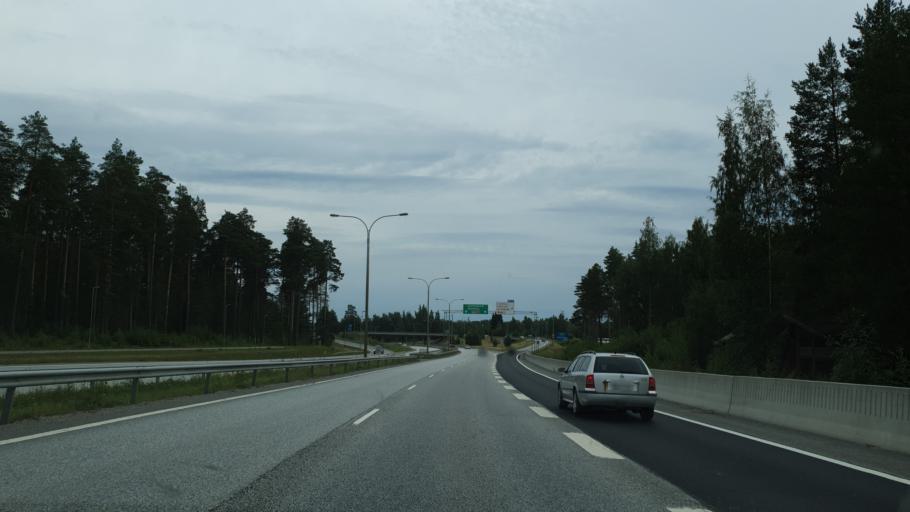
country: FI
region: North Karelia
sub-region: Joensuu
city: Joensuu
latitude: 62.6058
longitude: 29.7918
